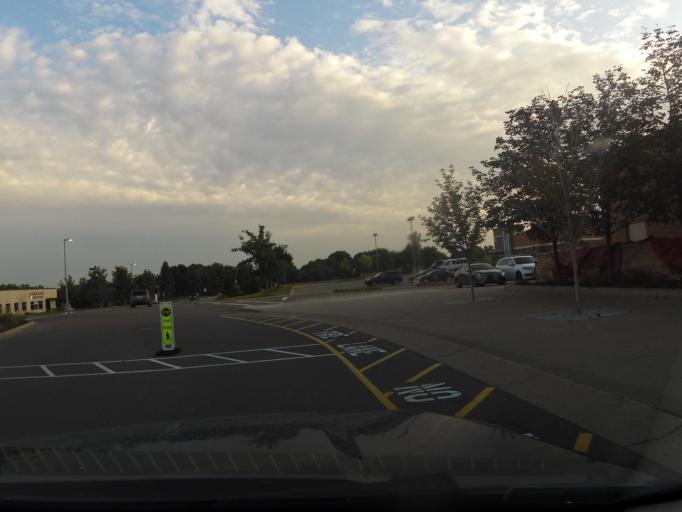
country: US
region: Minnesota
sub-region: Washington County
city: Woodbury
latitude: 44.9393
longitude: -92.9088
